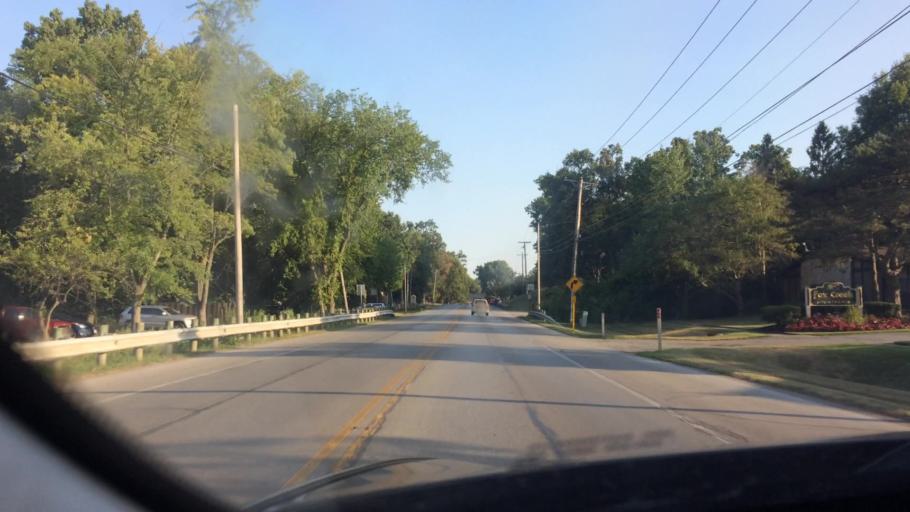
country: US
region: Ohio
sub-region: Lucas County
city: Holland
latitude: 41.6578
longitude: -83.7022
